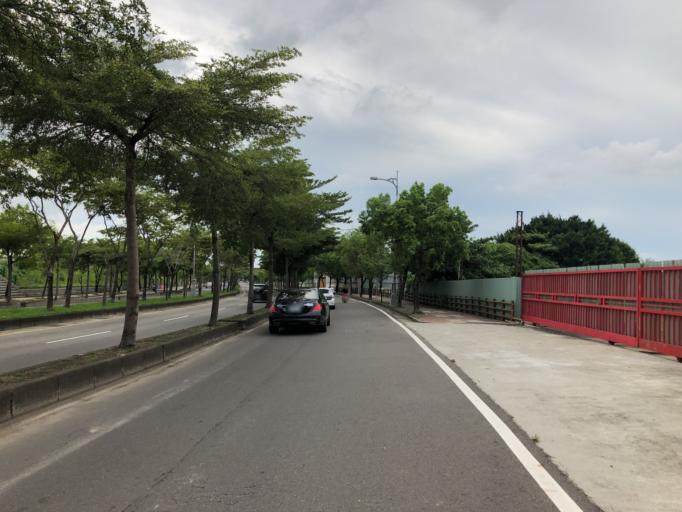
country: TW
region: Taiwan
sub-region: Taichung City
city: Taichung
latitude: 24.0905
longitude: 120.6527
